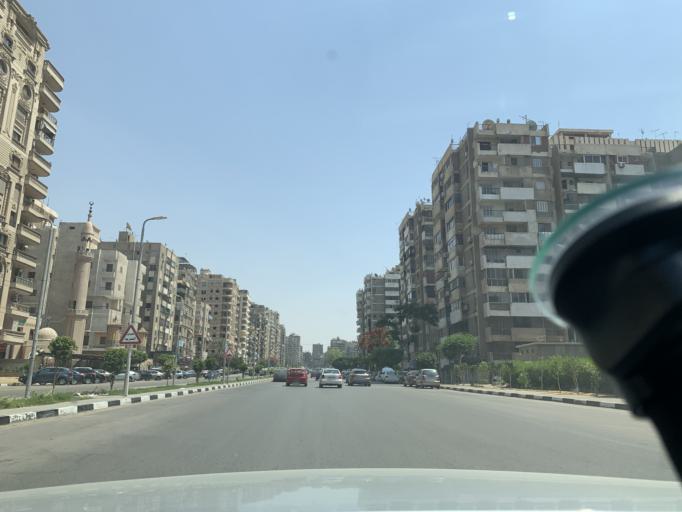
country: EG
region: Muhafazat al Qahirah
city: Cairo
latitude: 30.0674
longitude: 31.3488
